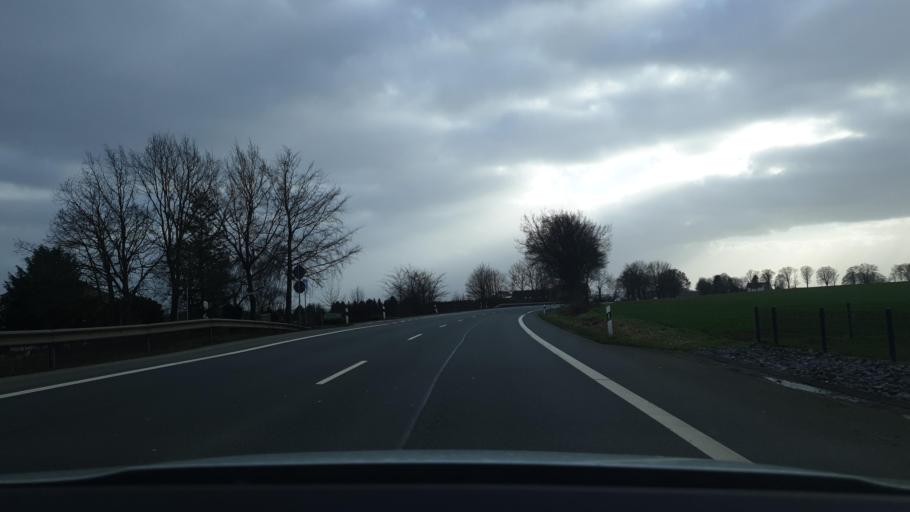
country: DE
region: North Rhine-Westphalia
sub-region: Regierungsbezirk Detmold
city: Huellhorst
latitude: 52.2615
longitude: 8.6365
